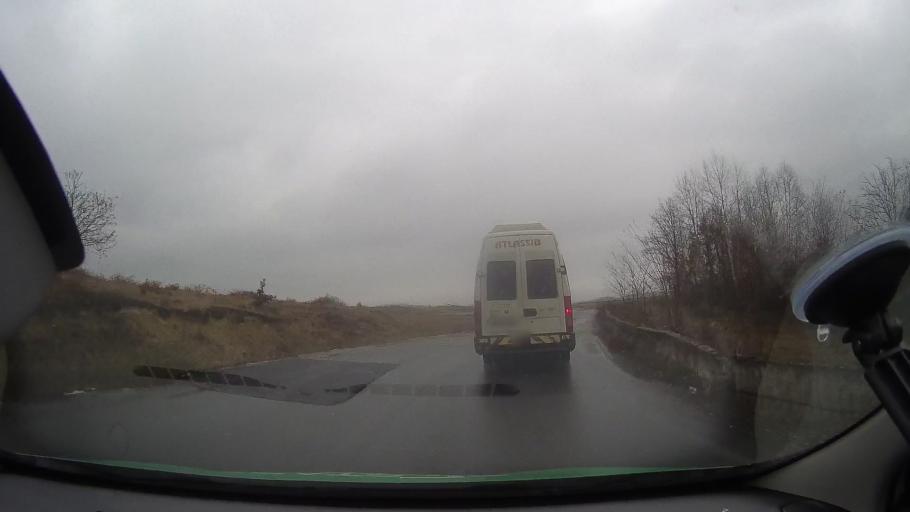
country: RO
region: Arad
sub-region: Comuna Halmagiu
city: Halmagiu
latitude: 46.2864
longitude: 22.5540
